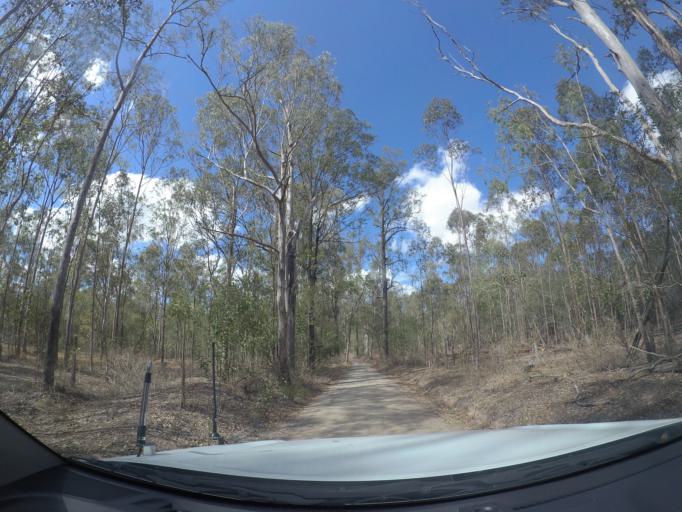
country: AU
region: Queensland
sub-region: Logan
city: North Maclean
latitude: -27.8315
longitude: 152.9675
